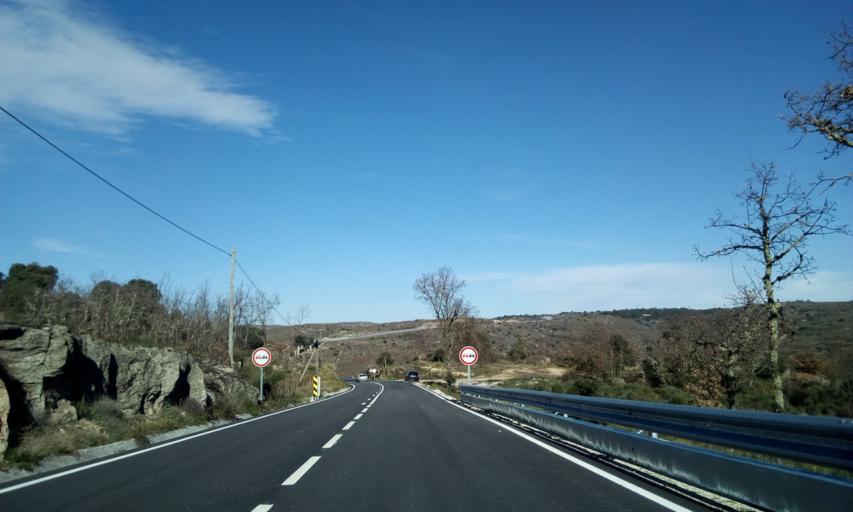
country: ES
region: Castille and Leon
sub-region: Provincia de Salamanca
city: Fuentes de Onoro
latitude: 40.6044
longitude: -6.9266
